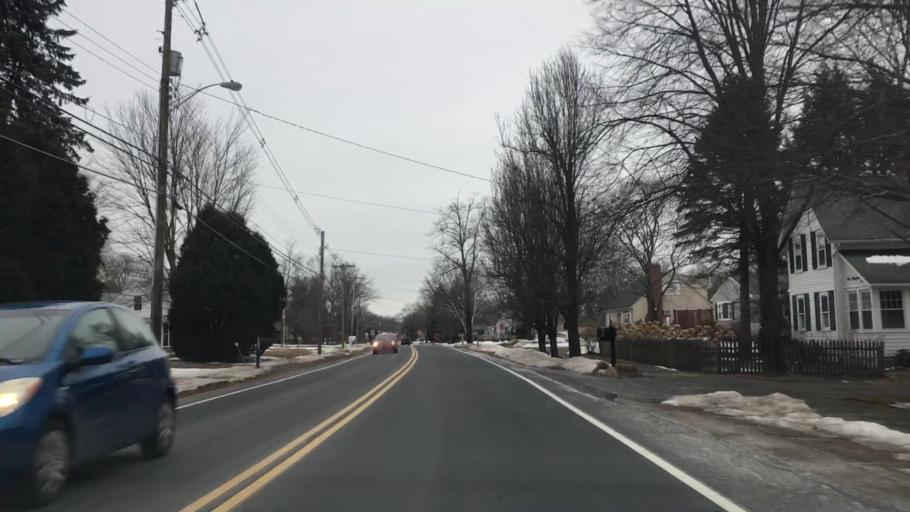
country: US
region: Massachusetts
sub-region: Hampden County
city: Agawam
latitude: 42.0723
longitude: -72.6783
